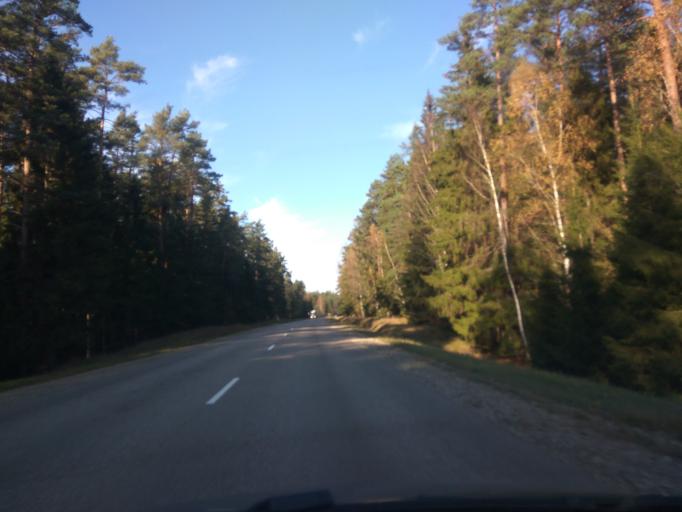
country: LV
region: Ventspils Rajons
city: Piltene
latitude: 57.0847
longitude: 21.7811
